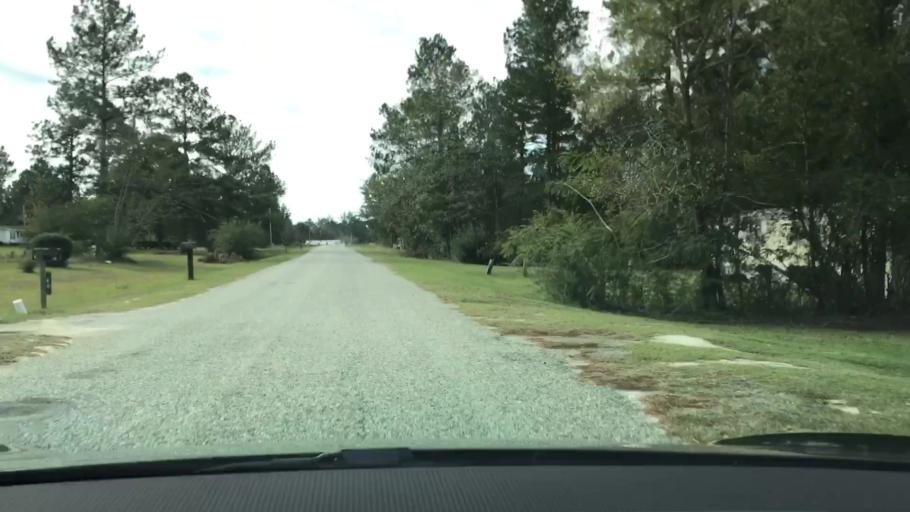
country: US
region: Georgia
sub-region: Jefferson County
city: Wadley
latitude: 32.8024
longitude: -82.3457
